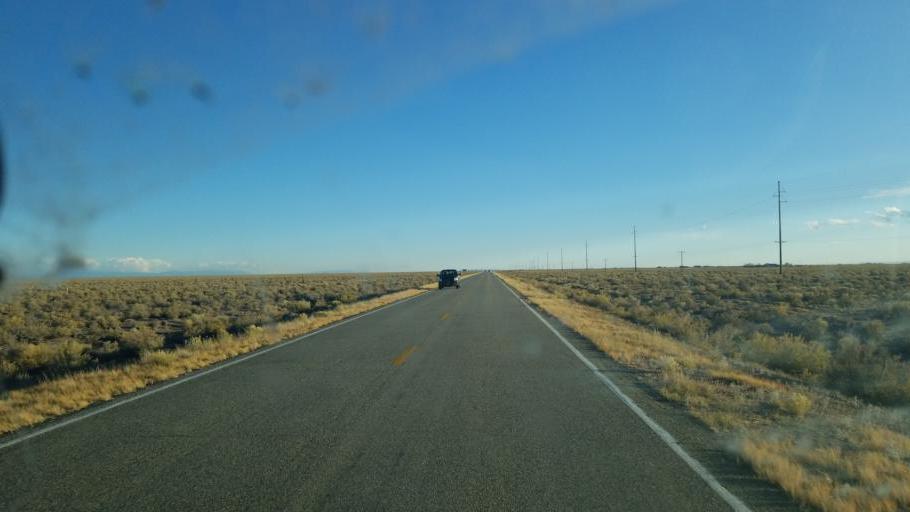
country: US
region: Colorado
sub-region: Saguache County
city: Center
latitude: 37.8663
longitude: -105.8938
